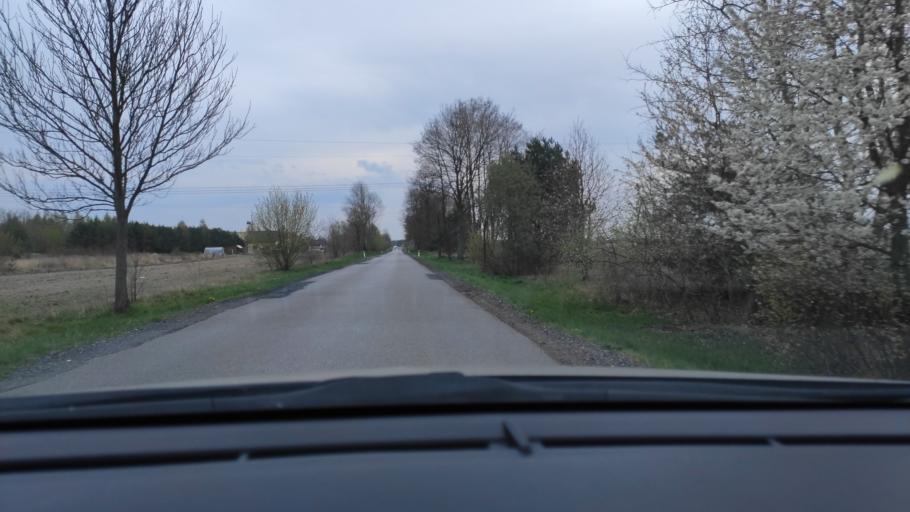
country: PL
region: Masovian Voivodeship
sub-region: Powiat zwolenski
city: Zwolen
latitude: 51.3687
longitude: 21.5638
